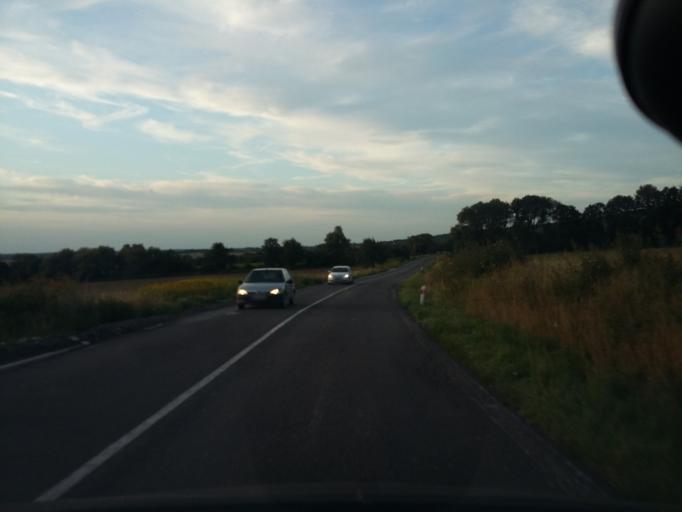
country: SK
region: Bratislavsky
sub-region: Okres Malacky
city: Malacky
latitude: 48.3770
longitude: 17.1487
